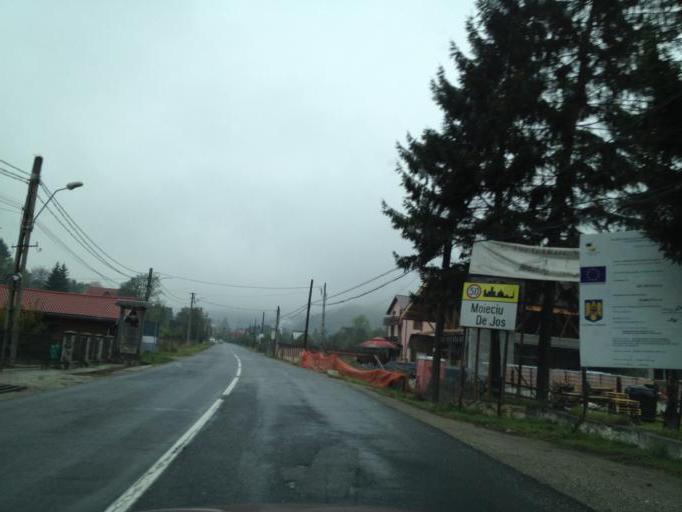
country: RO
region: Brasov
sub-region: Comuna Bran
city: Bran
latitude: 45.5102
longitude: 25.3524
